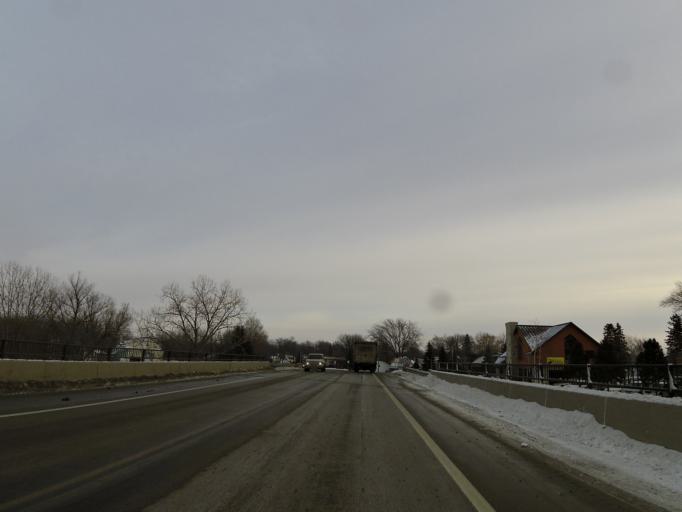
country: US
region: Minnesota
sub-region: Carver County
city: Victoria
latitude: 44.8599
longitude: -93.6660
